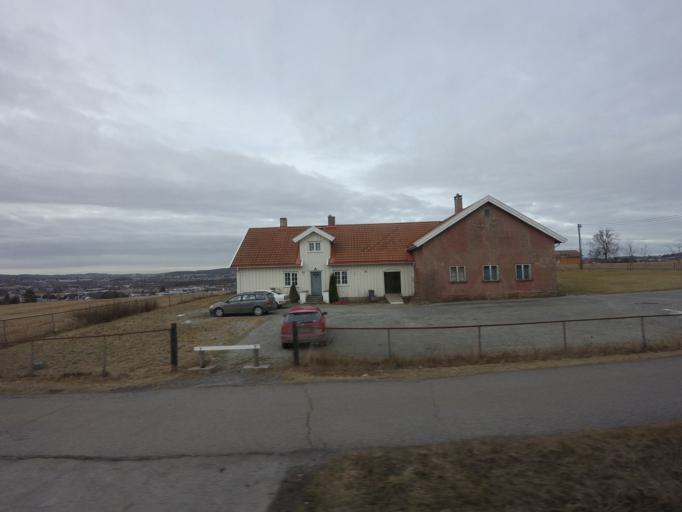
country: NO
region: Akershus
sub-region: Skedsmo
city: Lillestrom
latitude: 59.9790
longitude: 11.0556
